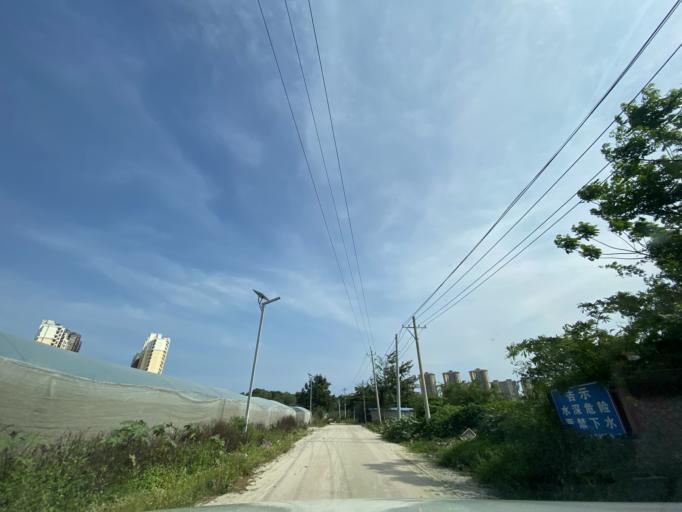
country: CN
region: Hainan
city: Yingzhou
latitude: 18.4058
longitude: 109.8370
